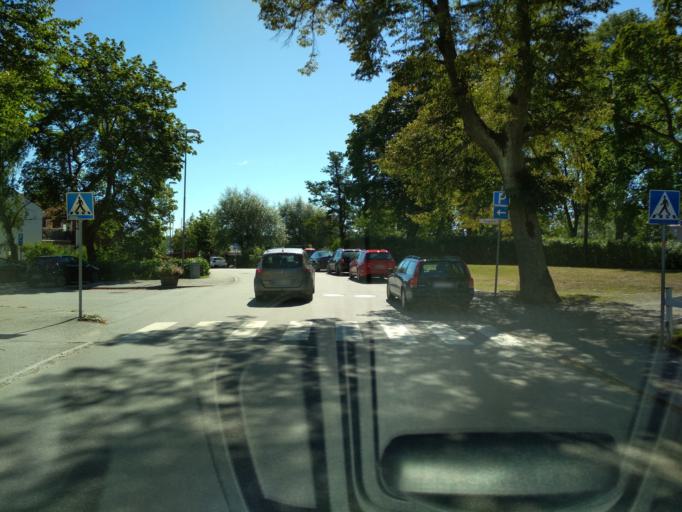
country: SE
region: Soedermanland
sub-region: Strangnas Kommun
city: Mariefred
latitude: 59.2589
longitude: 17.2201
